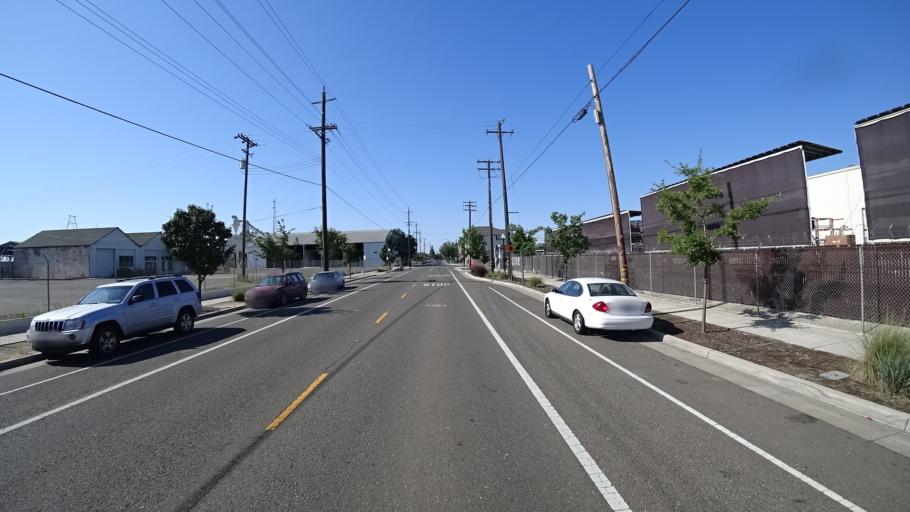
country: US
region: California
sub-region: Sacramento County
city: Florin
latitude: 38.5497
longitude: -121.4231
